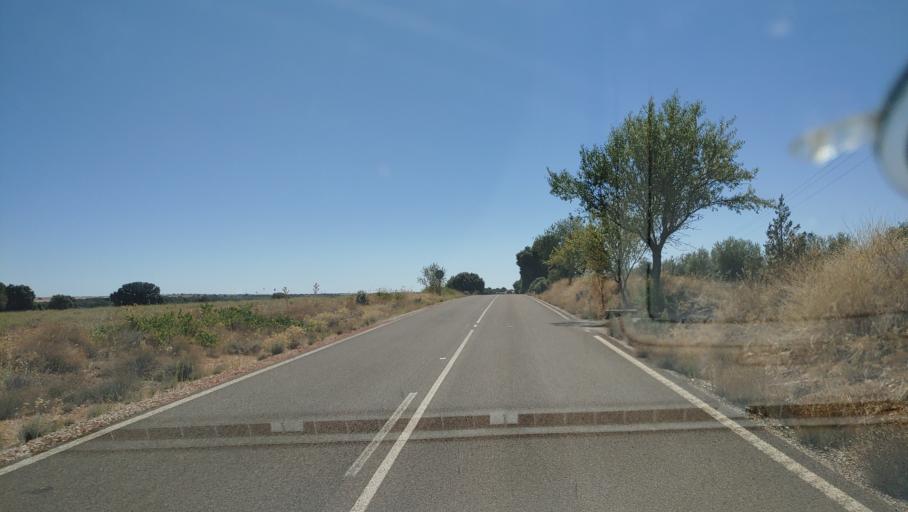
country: ES
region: Castille-La Mancha
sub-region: Provincia de Ciudad Real
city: Villahermosa
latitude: 38.8119
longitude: -2.8352
